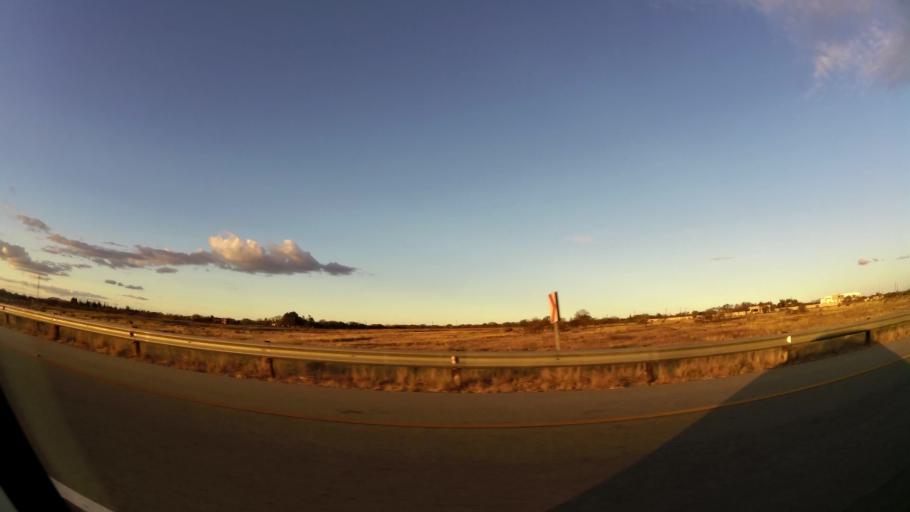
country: ZA
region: Limpopo
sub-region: Capricorn District Municipality
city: Polokwane
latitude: -23.8383
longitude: 29.5032
